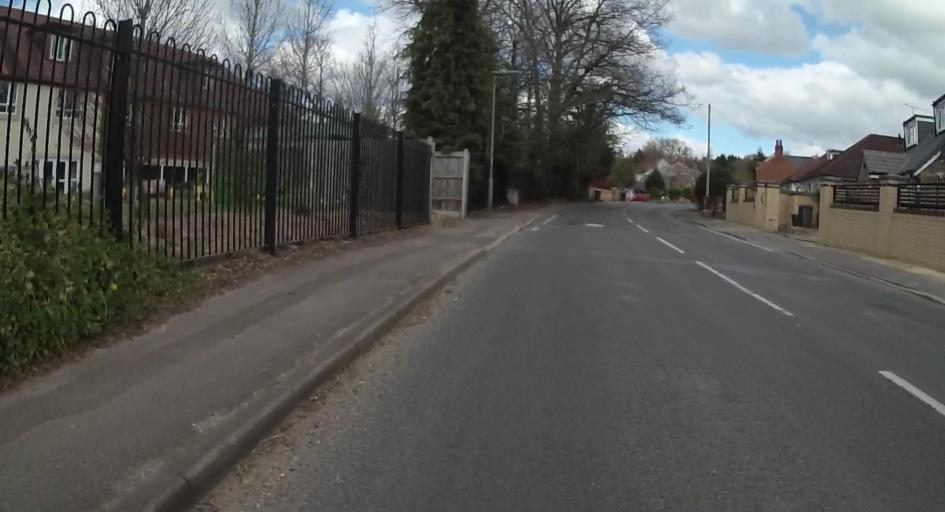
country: GB
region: England
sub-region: Surrey
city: Ottershaw
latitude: 51.3565
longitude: -0.5140
